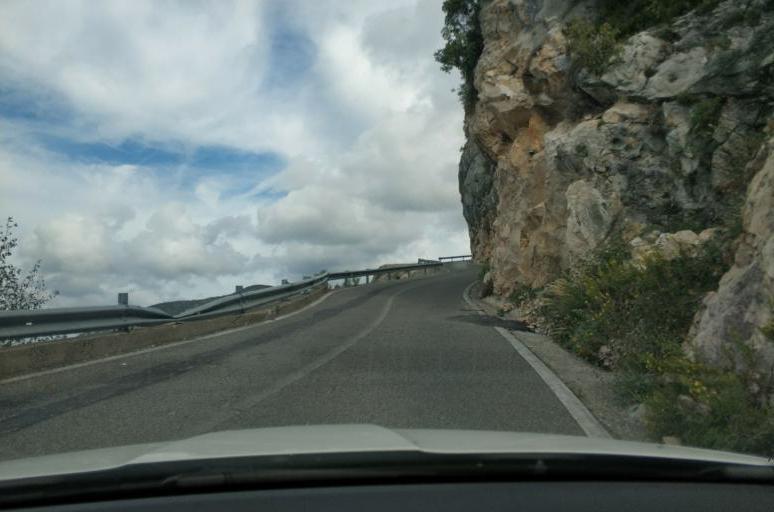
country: AL
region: Durres
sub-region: Rrethi i Krujes
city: Kruje
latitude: 41.5270
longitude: 19.7940
